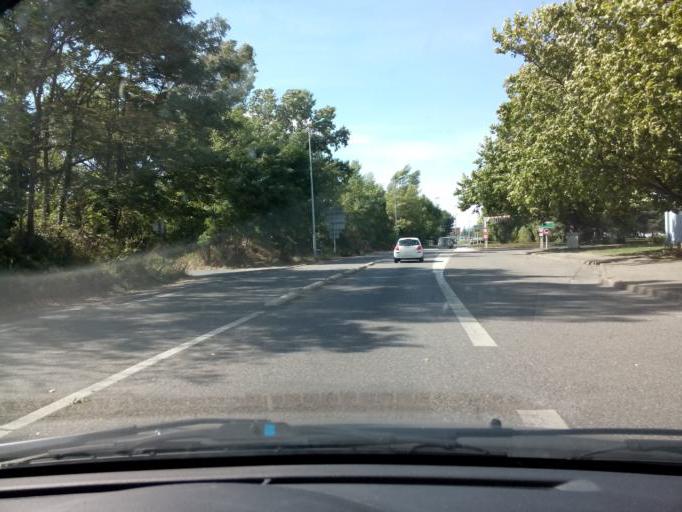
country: FR
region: Rhone-Alpes
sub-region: Departement du Rhone
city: Bron
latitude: 45.7205
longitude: 4.9233
